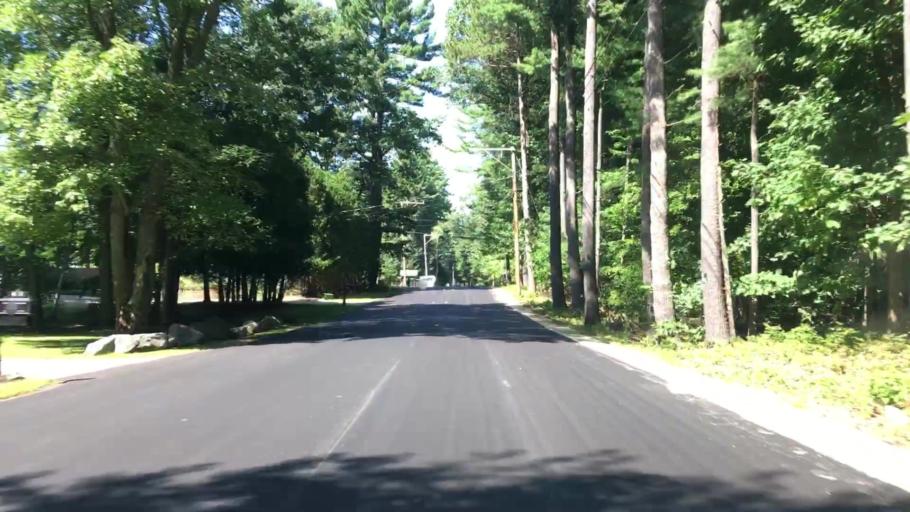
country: US
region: Maine
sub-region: York County
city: Eliot
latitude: 43.1631
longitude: -70.8398
